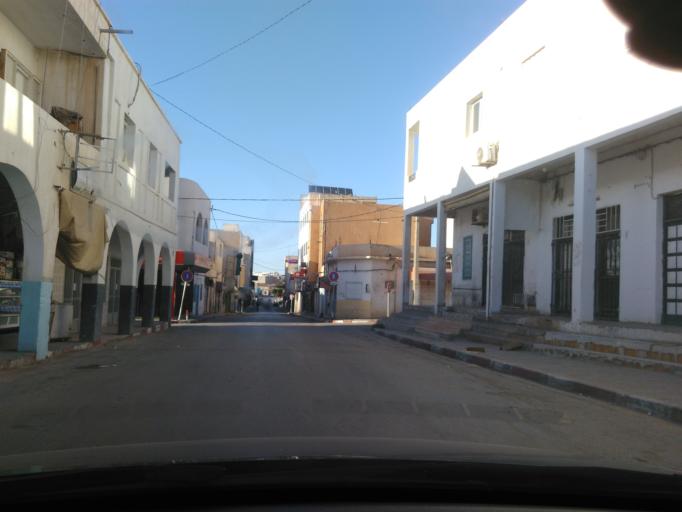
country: TN
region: Tataouine
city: Tataouine
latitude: 32.9272
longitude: 10.4484
